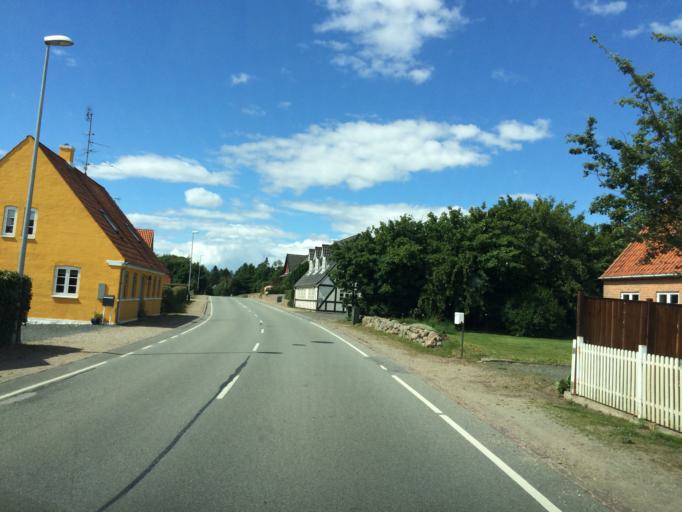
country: DK
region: South Denmark
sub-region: Faaborg-Midtfyn Kommune
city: Faaborg
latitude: 55.1354
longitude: 10.1990
